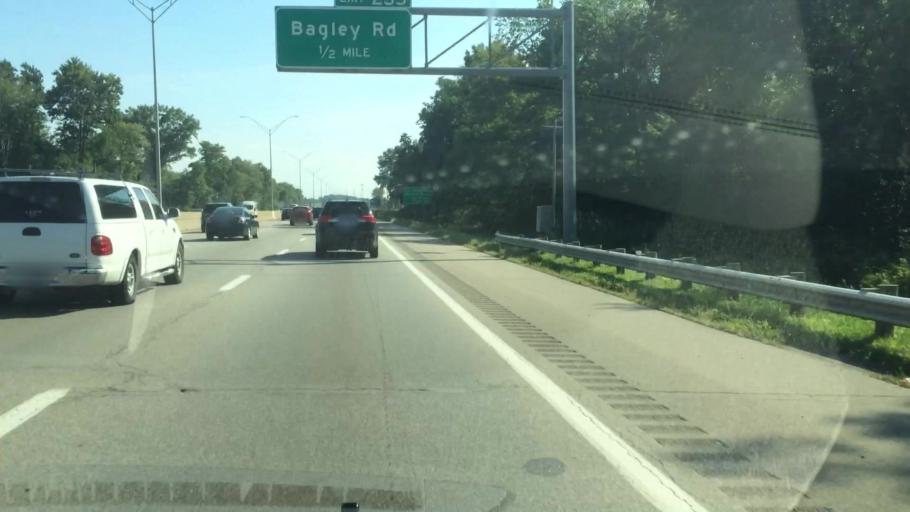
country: US
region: Ohio
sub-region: Cuyahoga County
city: Brook Park
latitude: 41.3845
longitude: -81.8179
